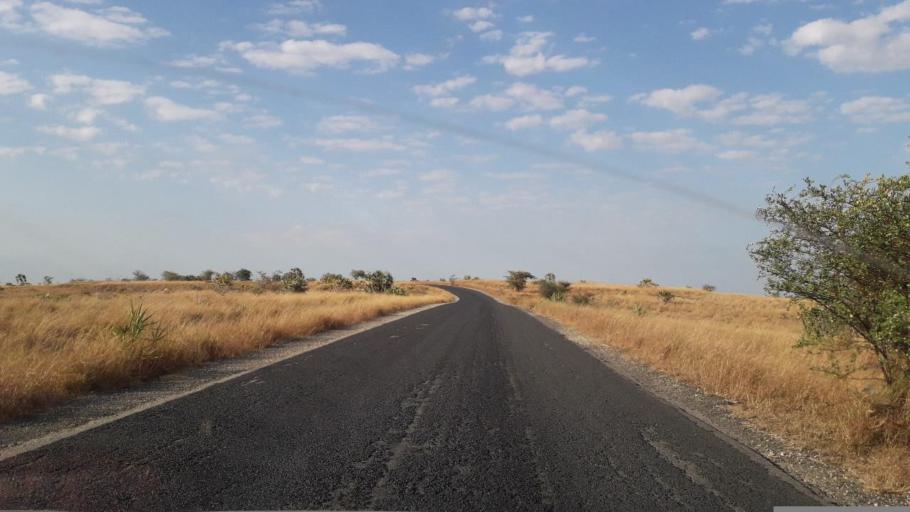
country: MG
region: Boeny
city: Mahajanga
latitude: -15.7914
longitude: 46.5123
